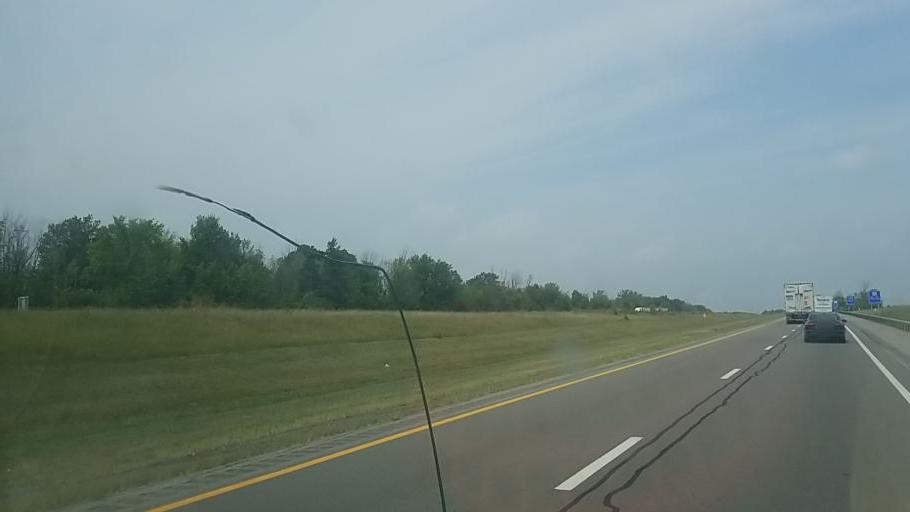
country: US
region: New York
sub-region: Erie County
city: Blasdell
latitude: 42.7735
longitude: -78.8161
